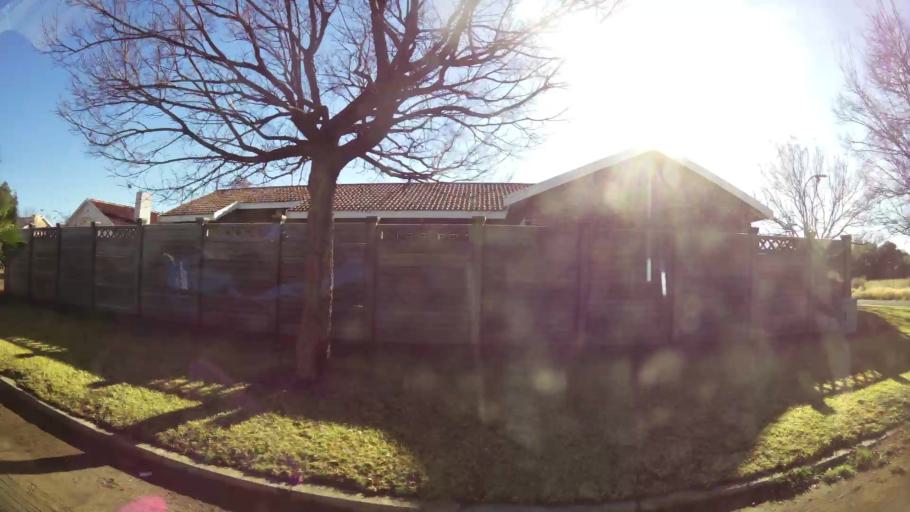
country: ZA
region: Northern Cape
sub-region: Frances Baard District Municipality
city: Kimberley
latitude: -28.7420
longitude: 24.7990
